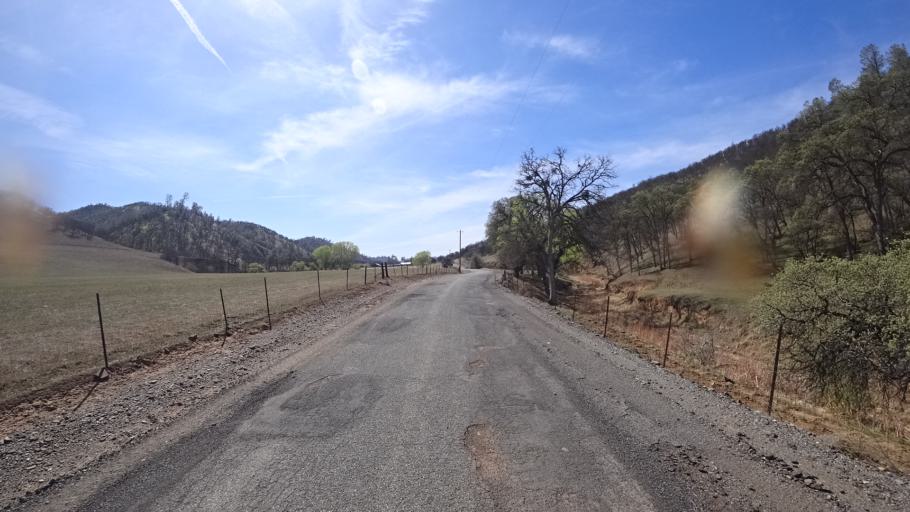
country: US
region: California
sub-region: Glenn County
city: Willows
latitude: 39.4959
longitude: -122.4541
